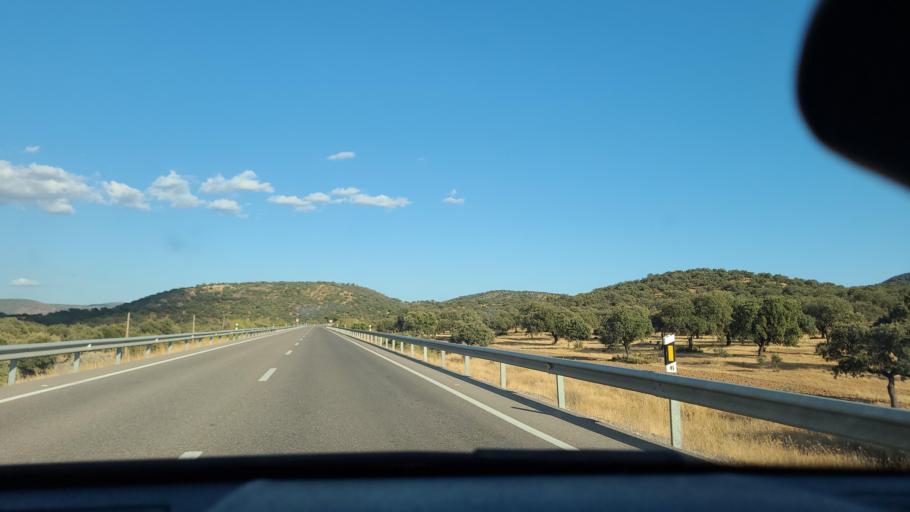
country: ES
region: Andalusia
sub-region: Province of Cordoba
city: Espiel
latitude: 38.2030
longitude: -5.1117
